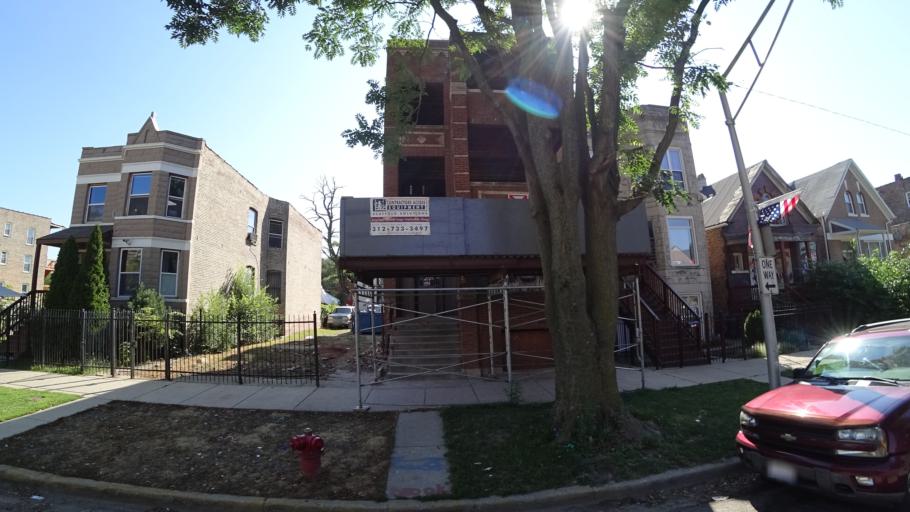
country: US
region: Illinois
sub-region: Cook County
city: Cicero
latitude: 41.8579
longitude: -87.7212
